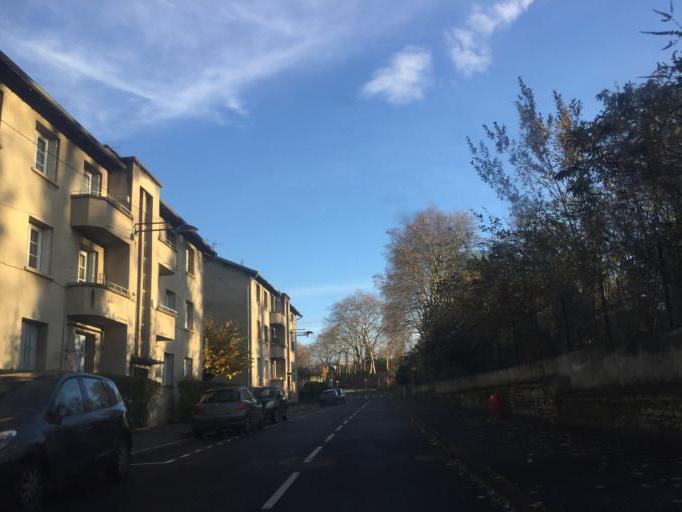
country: FR
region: Rhone-Alpes
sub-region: Departement du Rhone
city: Sathonay-Camp
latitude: 45.8274
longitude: 4.8698
